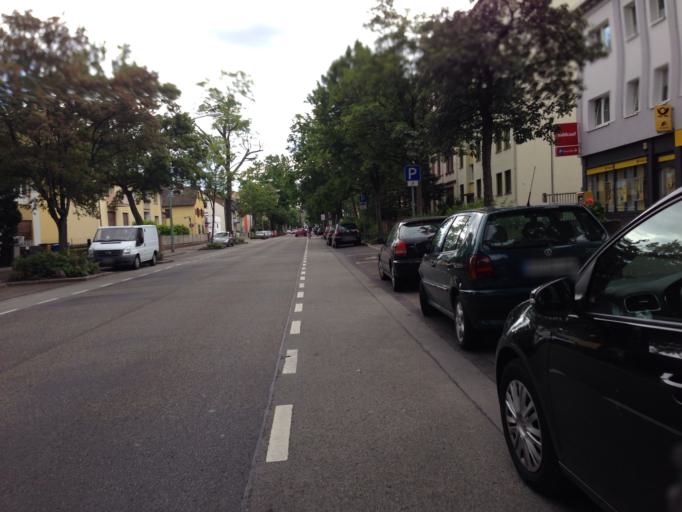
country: DE
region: Hesse
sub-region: Regierungsbezirk Darmstadt
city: Hanau am Main
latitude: 50.1327
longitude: 8.8895
